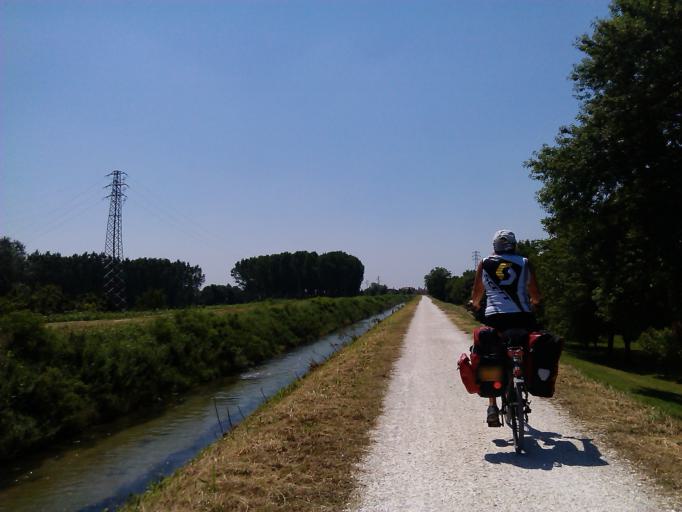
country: IT
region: Veneto
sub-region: Provincia di Padova
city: Camposampiero
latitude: 45.5749
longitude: 11.9399
